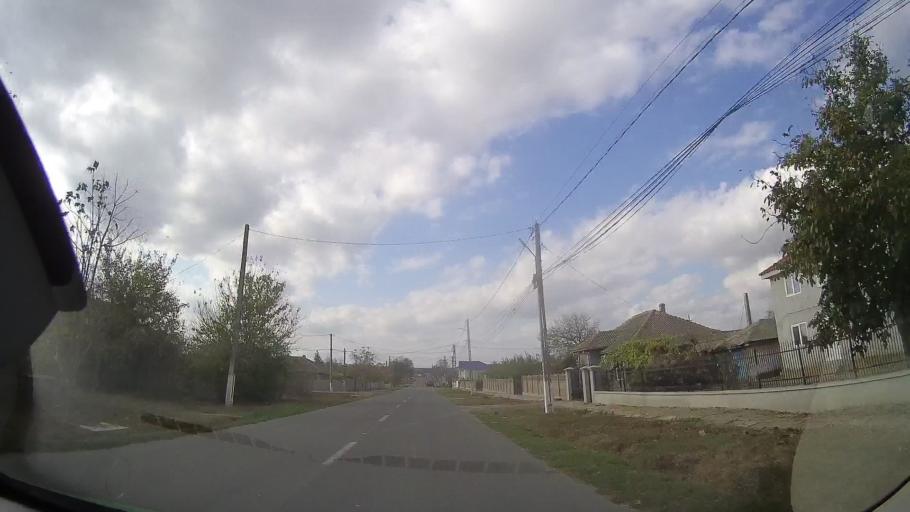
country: RO
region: Constanta
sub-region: Comuna Pecineaga
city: Pecineaga
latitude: 43.8952
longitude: 28.5021
